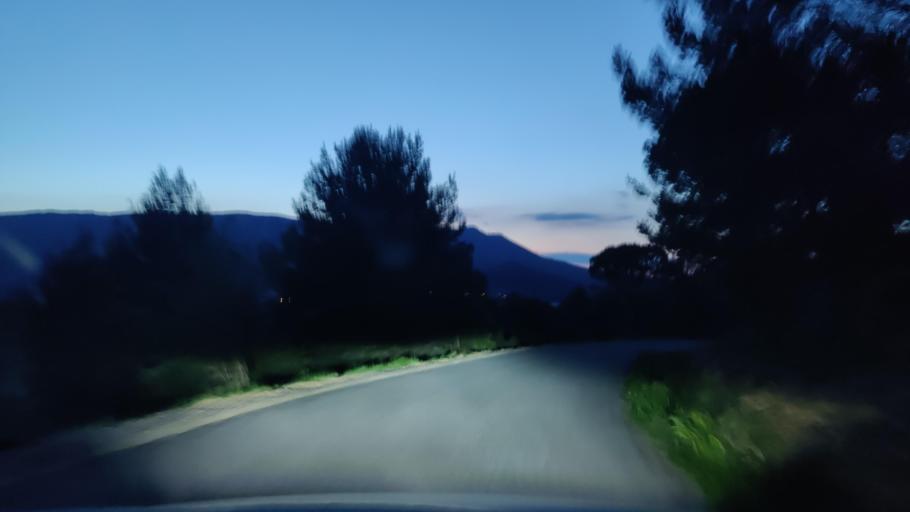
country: FR
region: Languedoc-Roussillon
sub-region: Departement des Pyrenees-Orientales
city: Estagel
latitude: 42.8791
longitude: 2.7398
